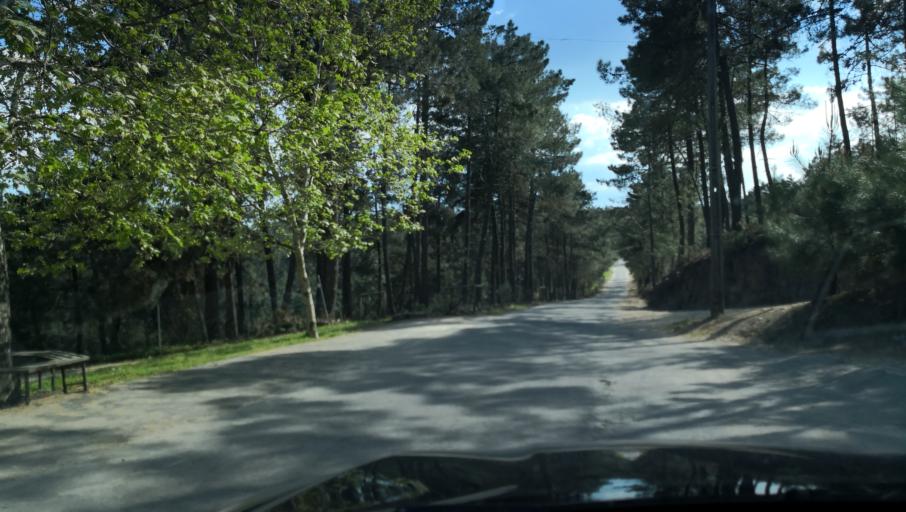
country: PT
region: Vila Real
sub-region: Sabrosa
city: Vilela
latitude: 41.2319
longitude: -7.6702
